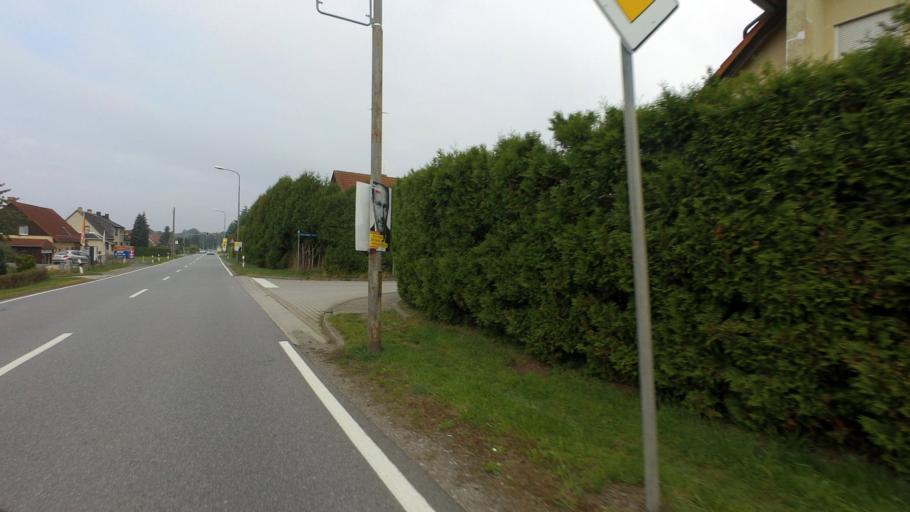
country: DE
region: Saxony
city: Arnsdorf
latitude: 51.0878
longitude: 14.0144
